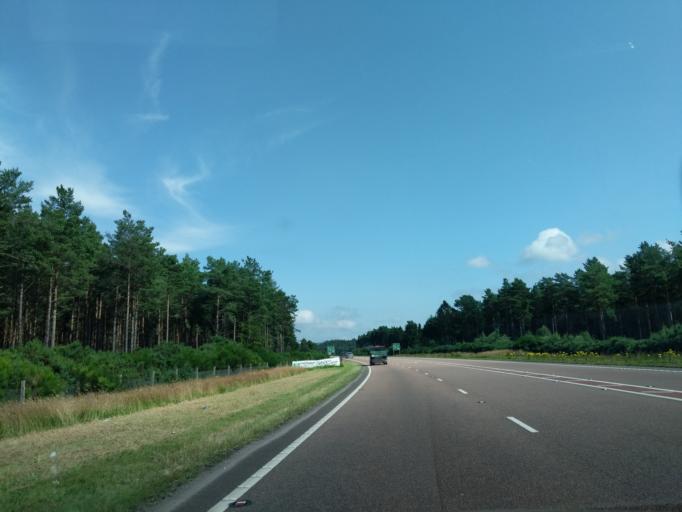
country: GB
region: Scotland
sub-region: Moray
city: Fochabers
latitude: 57.6235
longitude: -3.1346
